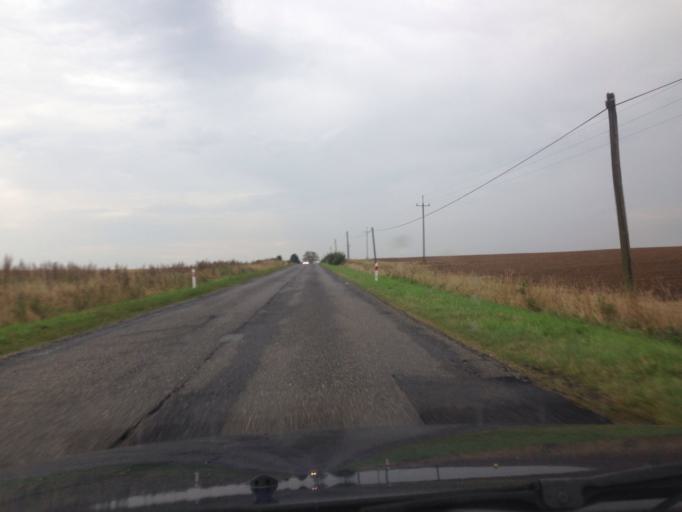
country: PL
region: Pomeranian Voivodeship
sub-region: Powiat bytowski
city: Czarna Dabrowka
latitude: 54.3640
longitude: 17.5160
